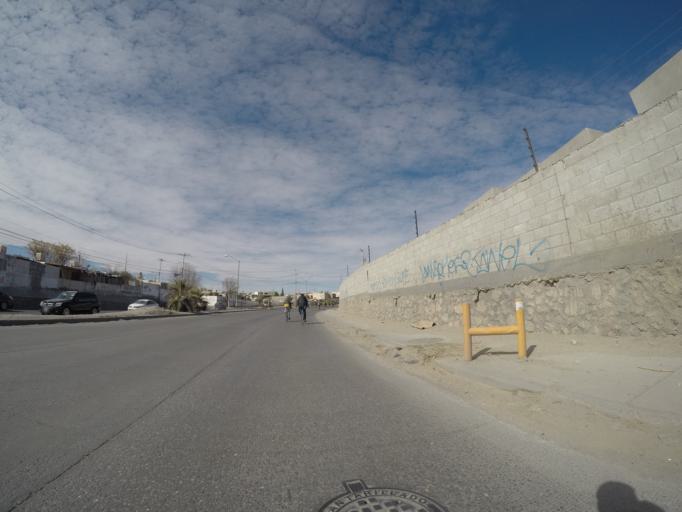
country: MX
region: Chihuahua
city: Ciudad Juarez
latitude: 31.6721
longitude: -106.4037
